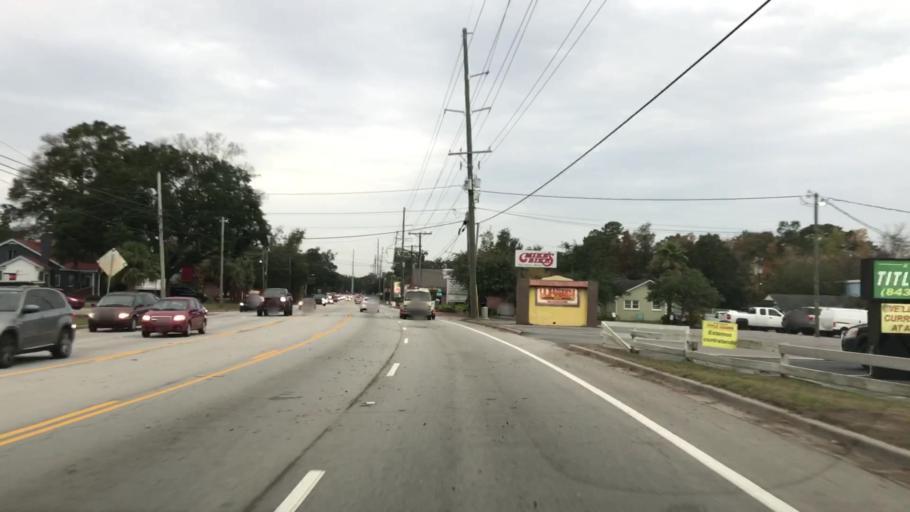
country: US
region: South Carolina
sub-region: Charleston County
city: Charleston
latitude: 32.7395
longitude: -79.9669
